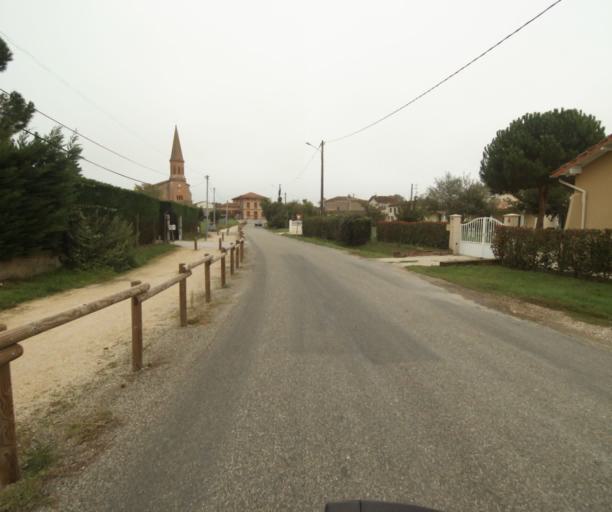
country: FR
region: Midi-Pyrenees
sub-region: Departement du Tarn-et-Garonne
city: Orgueil
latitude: 43.9036
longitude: 1.4095
